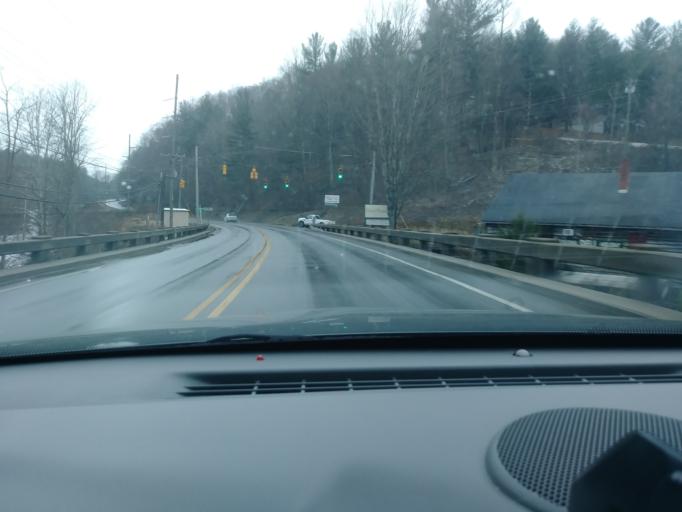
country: US
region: North Carolina
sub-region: Watauga County
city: Foscoe
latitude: 36.1944
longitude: -81.7452
